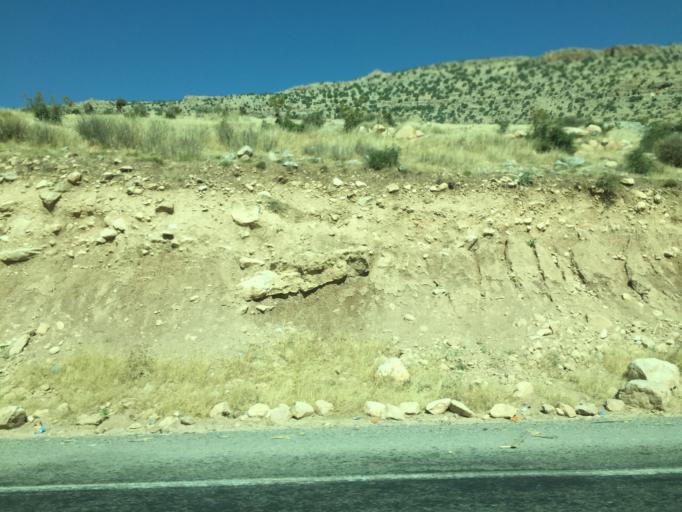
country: TR
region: Batman
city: Hasankeyf
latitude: 37.6879
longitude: 41.4547
